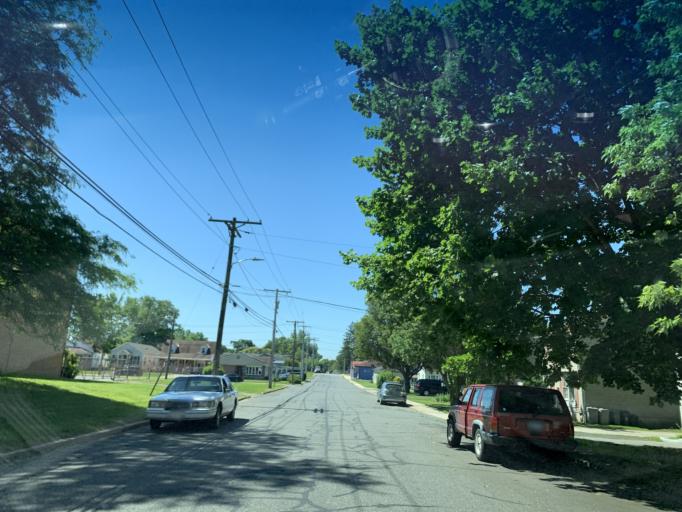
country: US
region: Maryland
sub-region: Harford County
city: Havre de Grace
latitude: 39.5452
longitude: -76.0952
